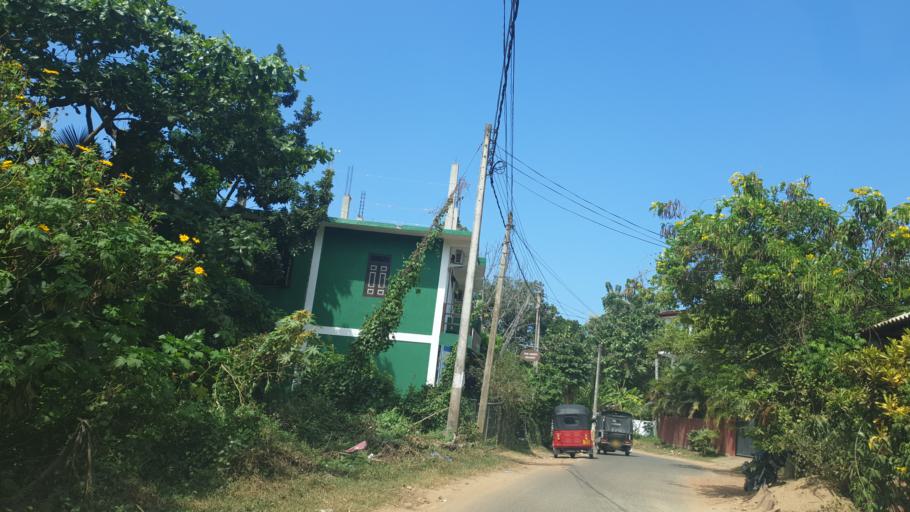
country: LK
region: Southern
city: Tangalla
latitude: 5.9661
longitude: 80.7082
